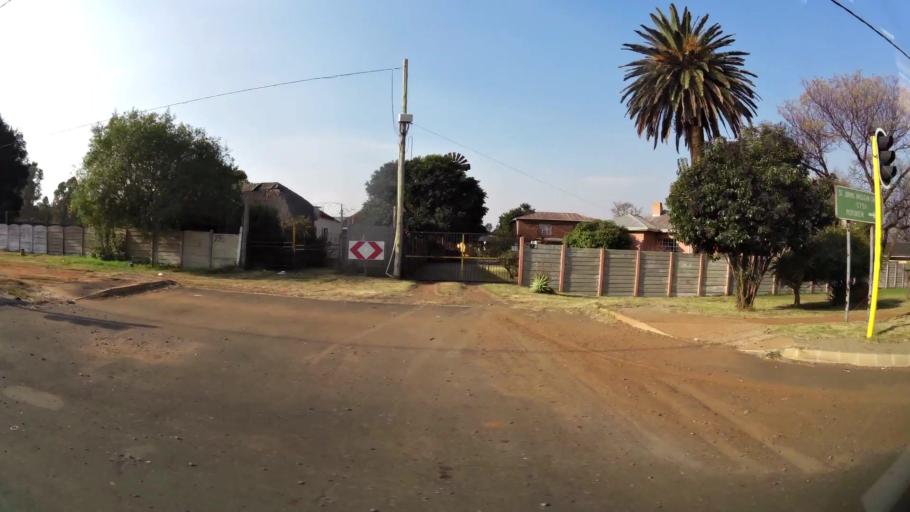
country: ZA
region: Gauteng
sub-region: Ekurhuleni Metropolitan Municipality
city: Benoni
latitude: -26.1280
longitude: 28.3855
